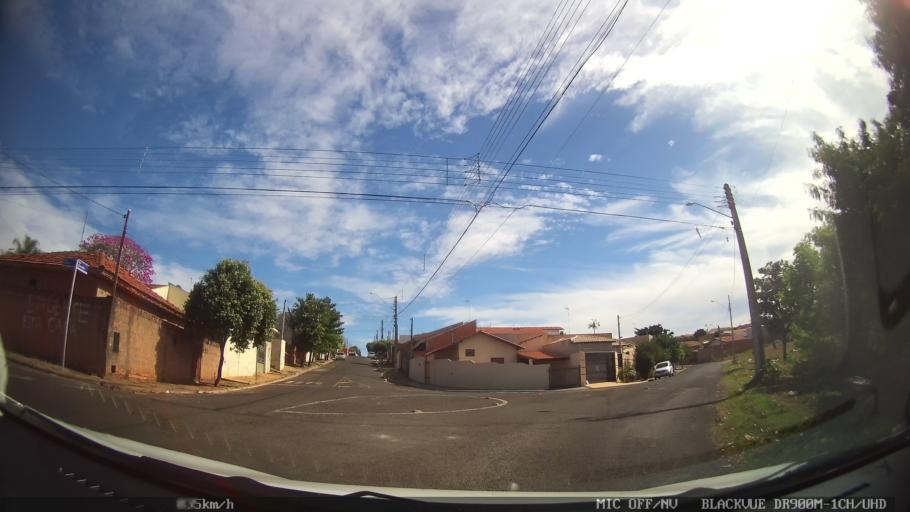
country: BR
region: Sao Paulo
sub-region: Catanduva
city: Catanduva
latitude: -21.1270
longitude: -48.9442
